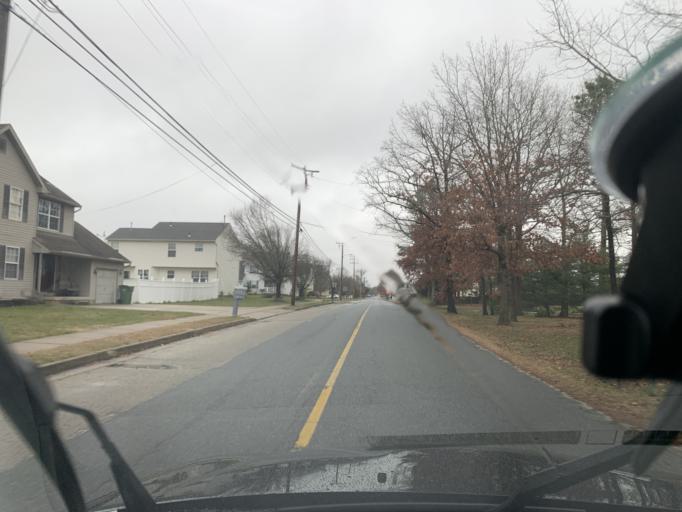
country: US
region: New Jersey
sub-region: Atlantic County
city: Pomona
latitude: 39.4298
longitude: -74.5874
